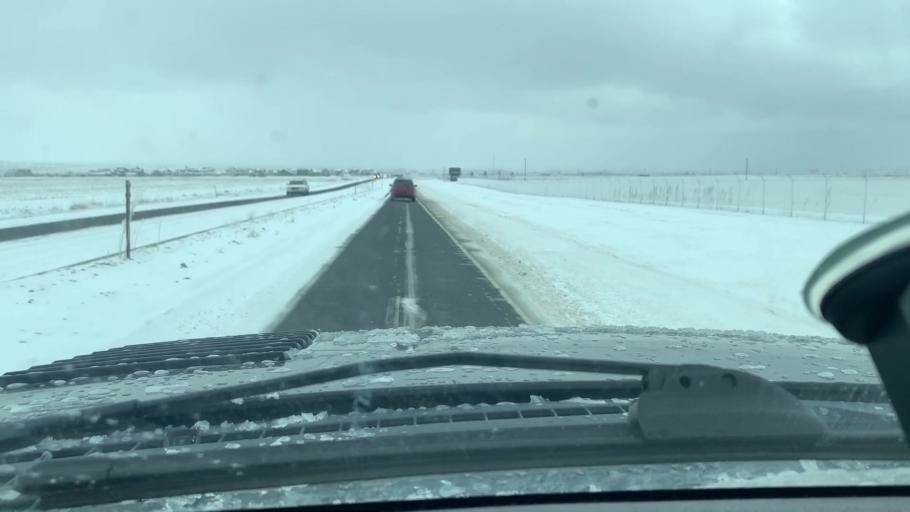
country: US
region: Colorado
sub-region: Weld County
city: Mead
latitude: 40.1963
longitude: -104.9702
